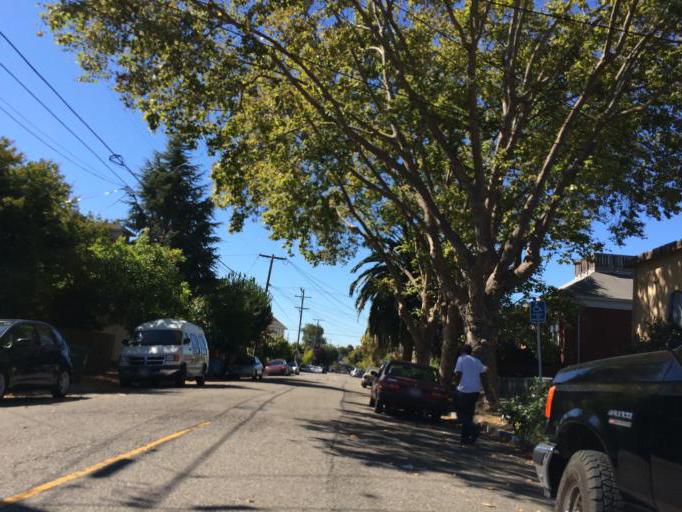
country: US
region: California
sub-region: Alameda County
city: Berkeley
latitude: 37.8584
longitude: -122.2733
